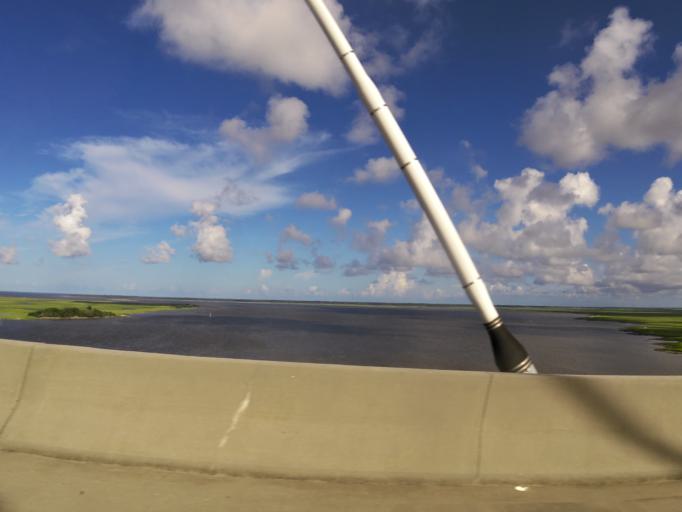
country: US
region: Georgia
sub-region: Glynn County
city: Brunswick
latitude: 31.1142
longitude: -81.4858
